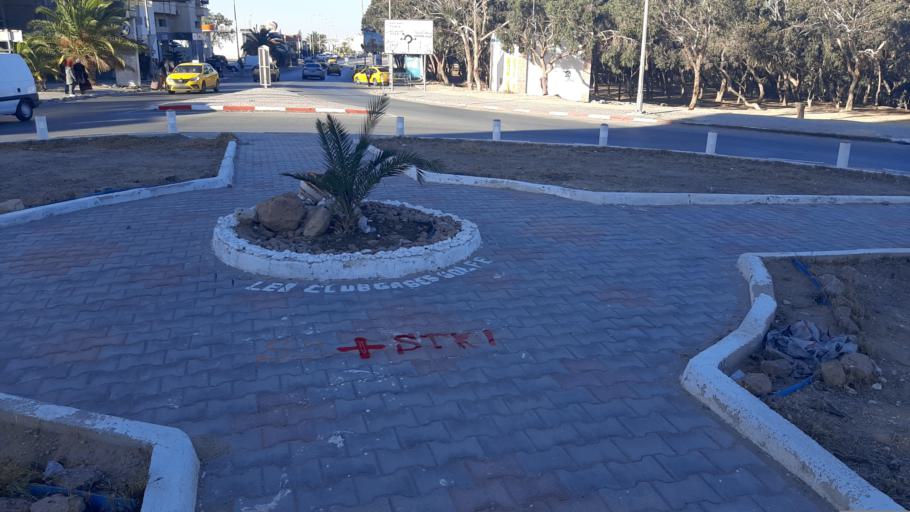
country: TN
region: Qabis
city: Gabes
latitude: 33.8549
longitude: 10.1070
